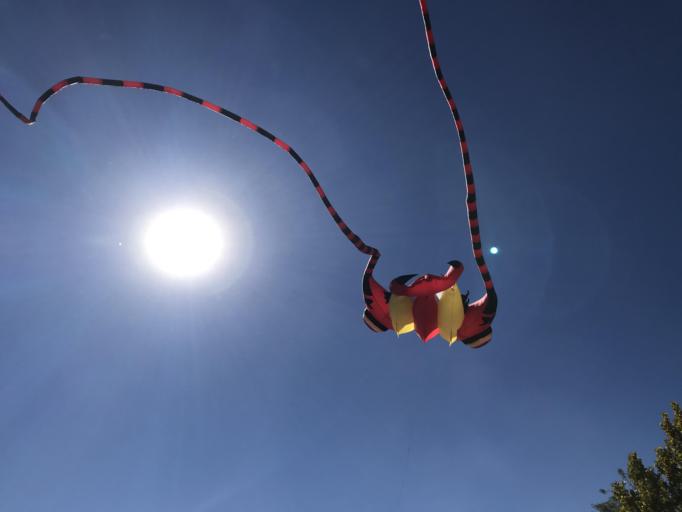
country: MX
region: Durango
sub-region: Durango
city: Sebastian Lerdo de Tejada
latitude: 23.9910
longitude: -104.6077
